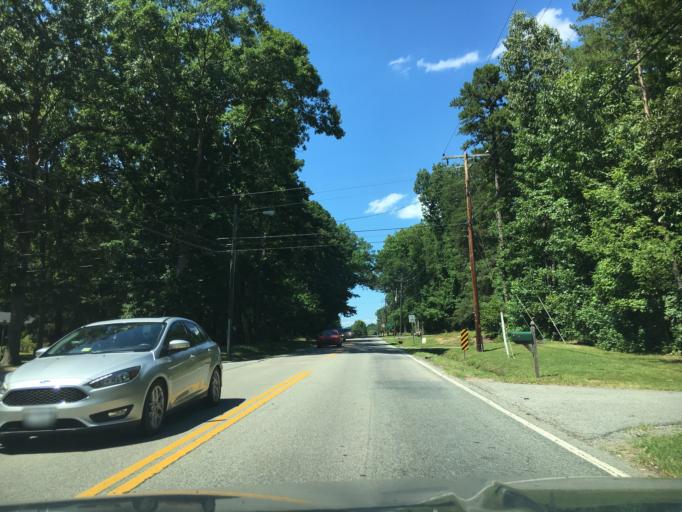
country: US
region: Virginia
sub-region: Halifax County
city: South Boston
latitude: 36.7284
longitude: -78.9061
